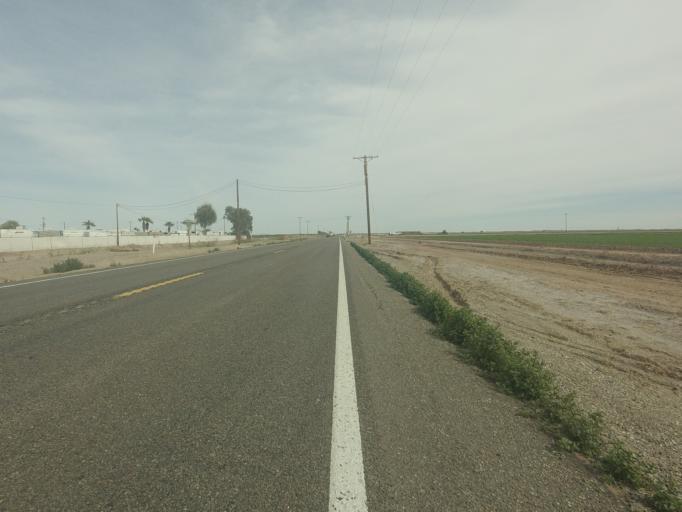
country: US
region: California
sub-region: Imperial County
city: Holtville
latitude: 32.9747
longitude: -115.3260
